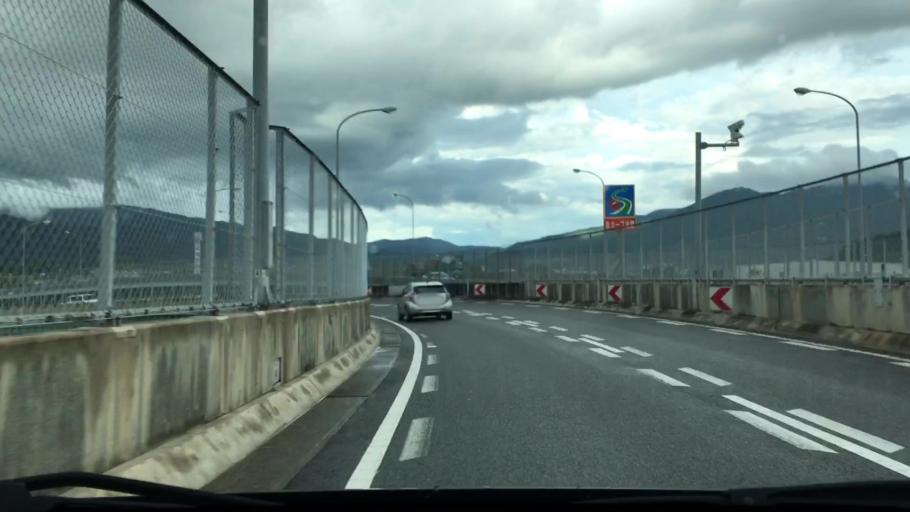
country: JP
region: Fukuoka
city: Umi
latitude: 33.6295
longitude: 130.4831
